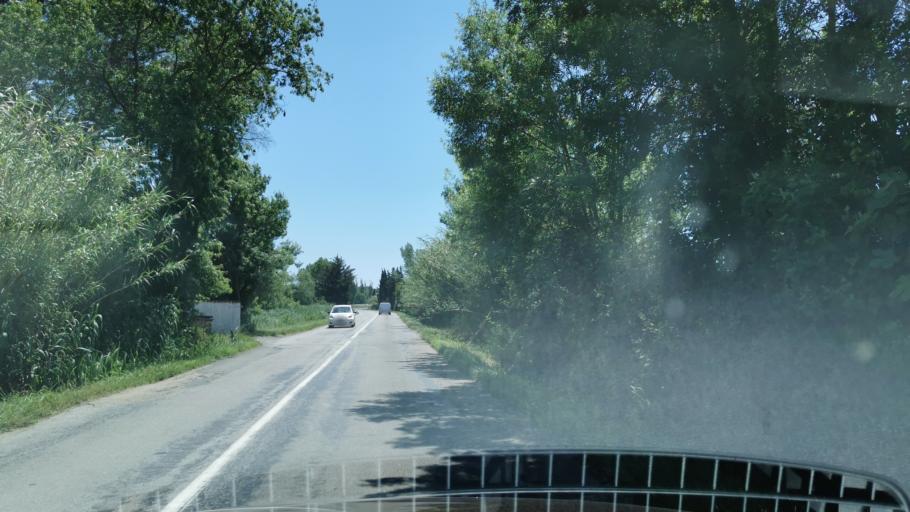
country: FR
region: Languedoc-Roussillon
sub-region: Departement de l'Aude
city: Narbonne
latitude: 43.2036
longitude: 3.0118
